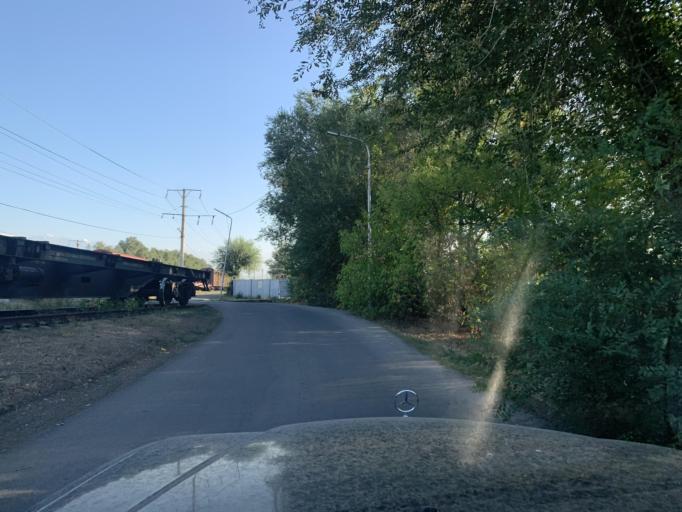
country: KZ
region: Almaty Oblysy
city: Energeticheskiy
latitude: 43.3888
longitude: 76.9988
